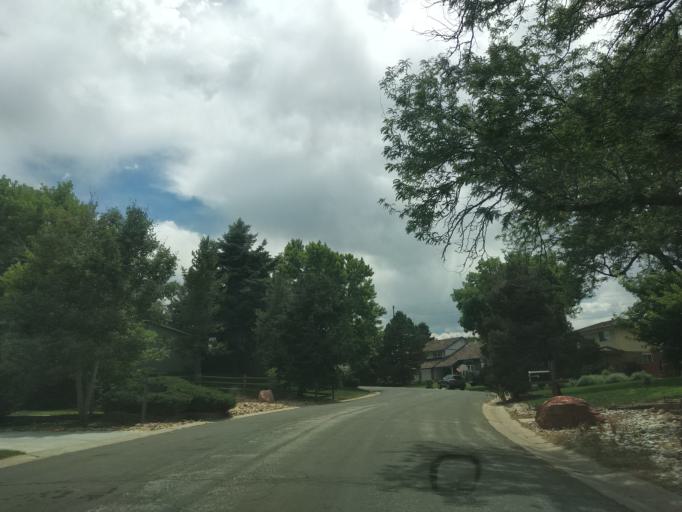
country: US
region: Colorado
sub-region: Jefferson County
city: Lakewood
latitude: 39.6848
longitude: -105.1273
